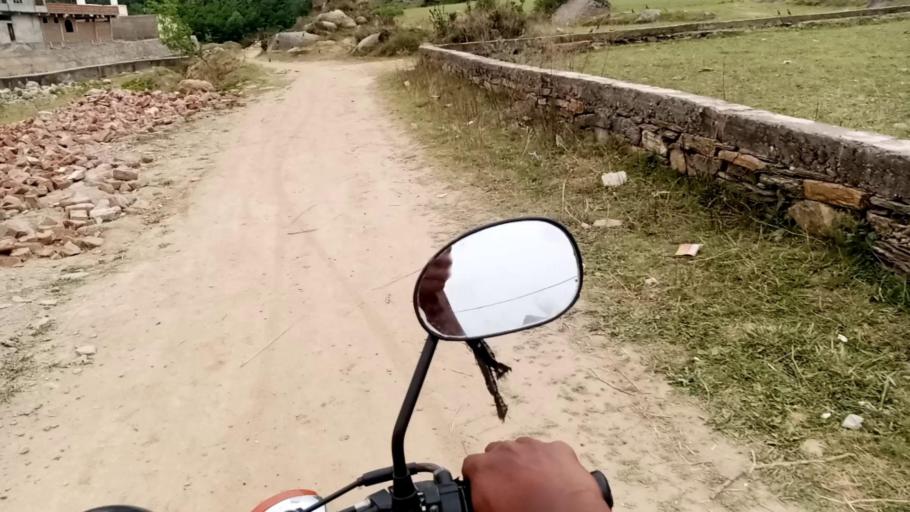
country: PK
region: Khyber Pakhtunkhwa
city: Saidu Sharif
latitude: 34.7535
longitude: 72.3870
